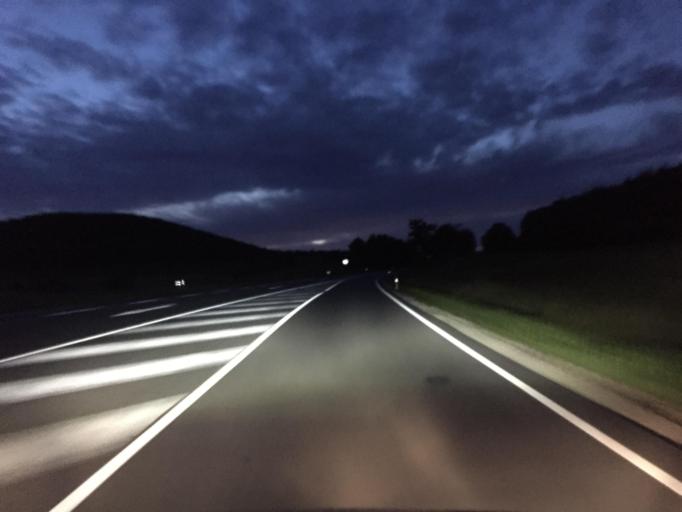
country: DE
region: Baden-Wuerttemberg
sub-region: Freiburg Region
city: Blumberg
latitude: 47.8765
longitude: 8.5362
